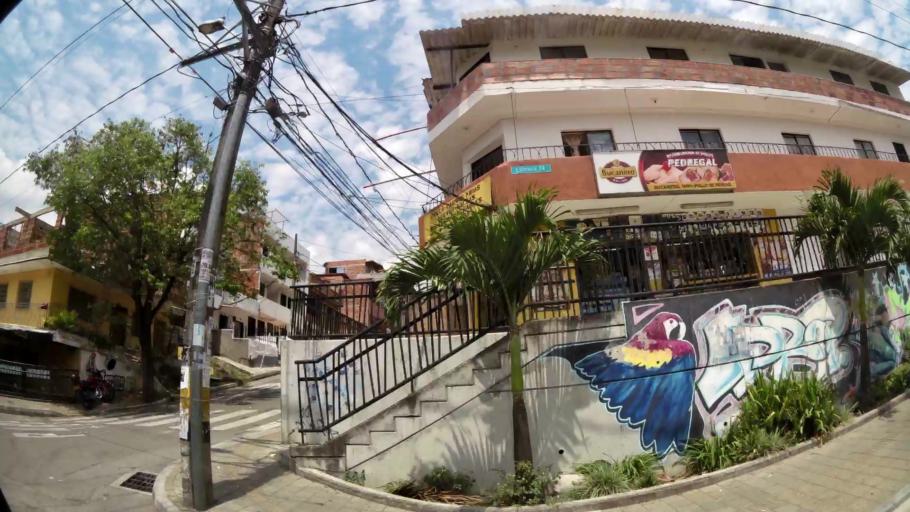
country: CO
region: Antioquia
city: Bello
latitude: 6.3029
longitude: -75.5718
